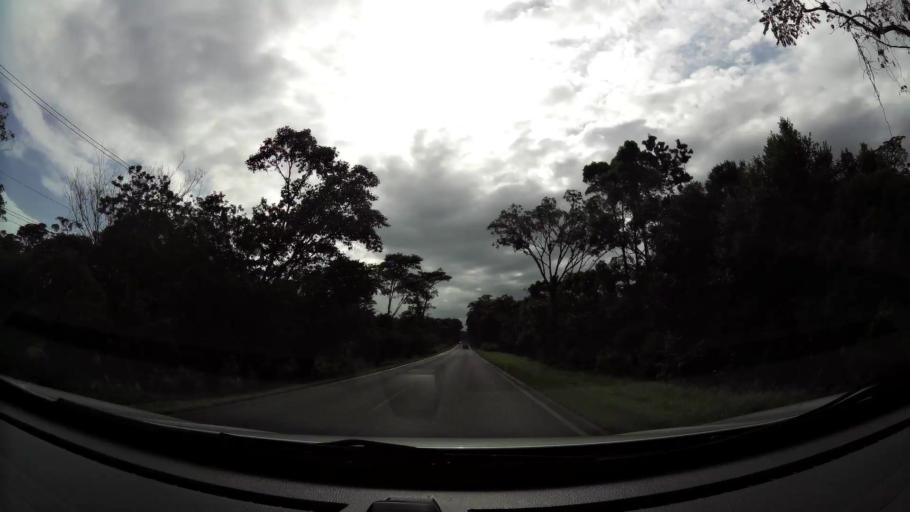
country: CR
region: Limon
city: Pocora
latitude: 10.1866
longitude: -83.6322
